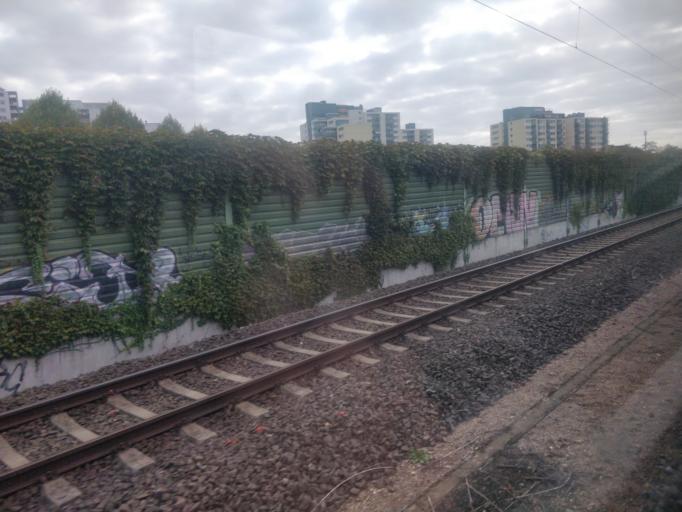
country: DE
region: North Rhine-Westphalia
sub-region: Regierungsbezirk Koln
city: Gremberghoven
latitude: 50.8980
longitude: 7.0560
